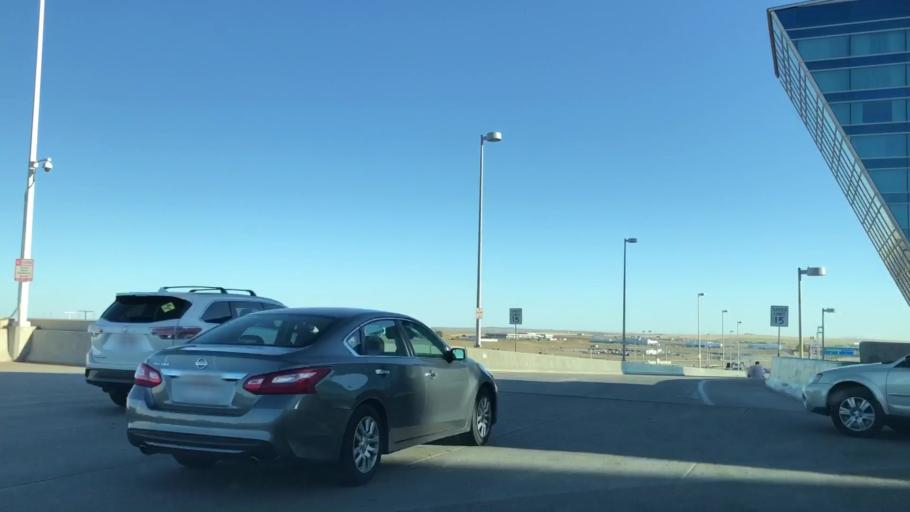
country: US
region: Colorado
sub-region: Weld County
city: Lochbuie
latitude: 39.8482
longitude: -104.6728
